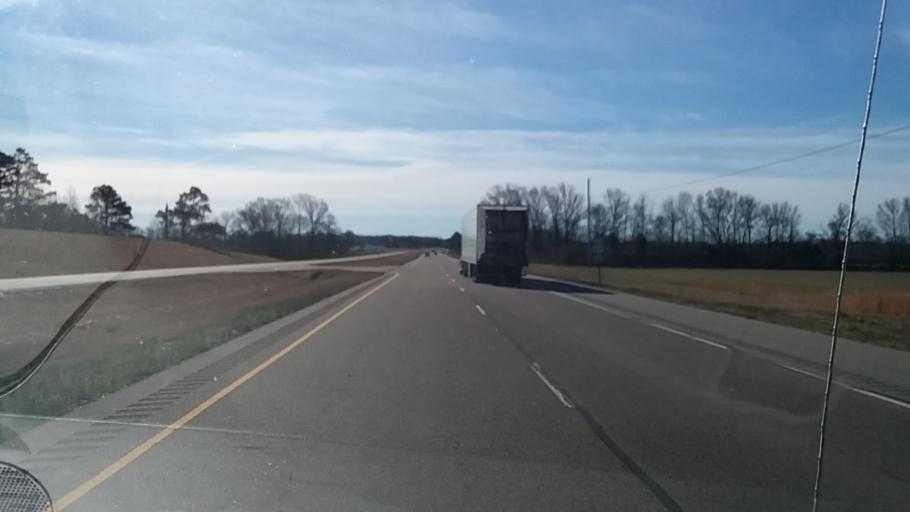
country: US
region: Tennessee
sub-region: Crockett County
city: Alamo
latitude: 35.8578
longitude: -89.2029
